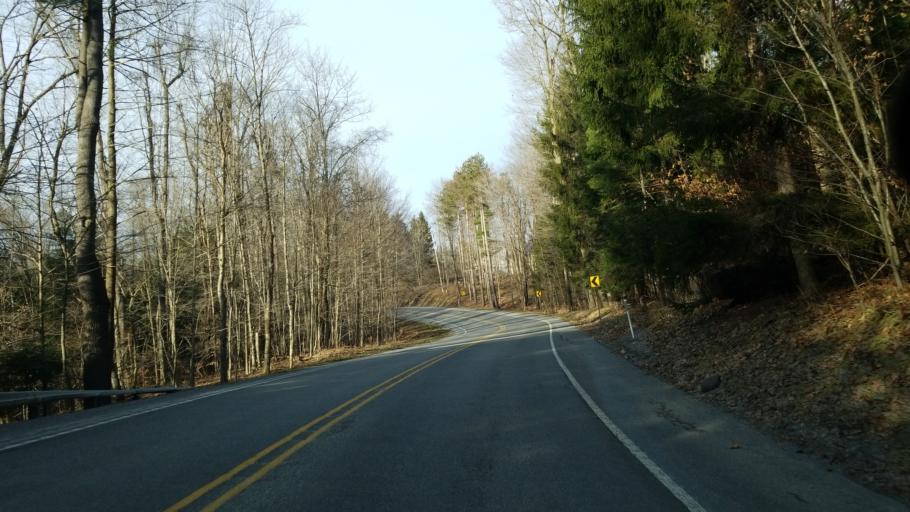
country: US
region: Pennsylvania
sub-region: Clearfield County
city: Curwensville
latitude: 40.9703
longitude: -78.6186
